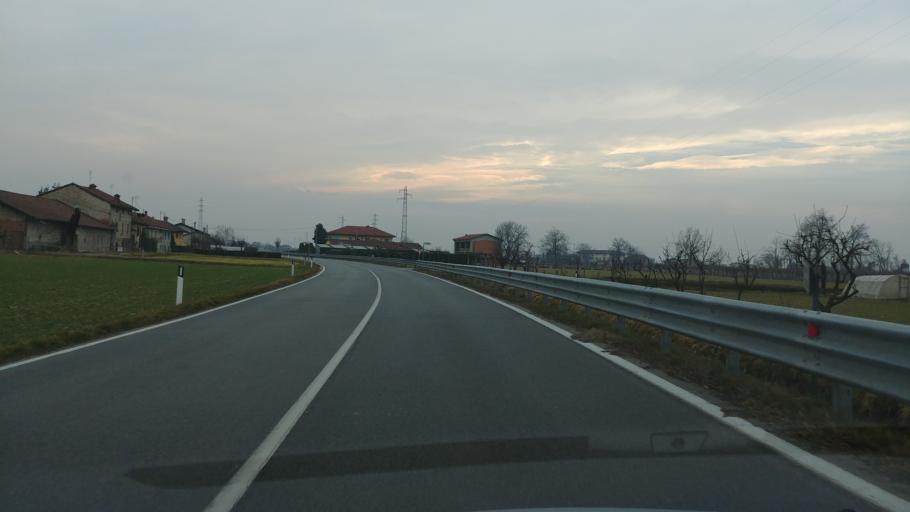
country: IT
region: Piedmont
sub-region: Provincia di Cuneo
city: Montanera
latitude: 44.4921
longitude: 7.6602
